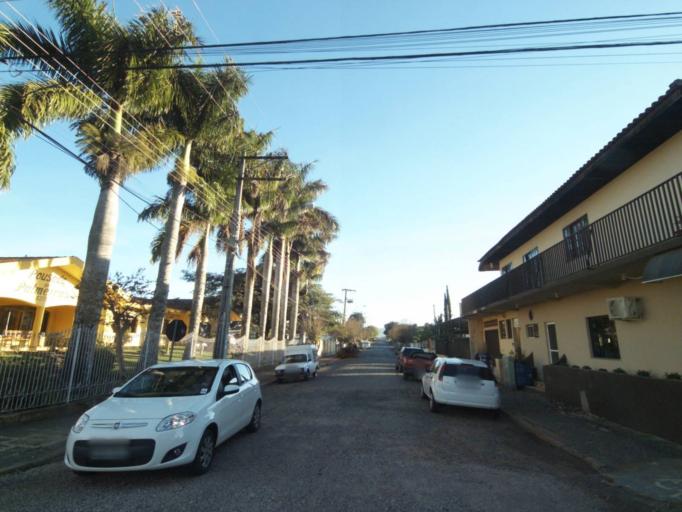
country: BR
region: Parana
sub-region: Tibagi
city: Tibagi
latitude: -24.5170
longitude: -50.4109
